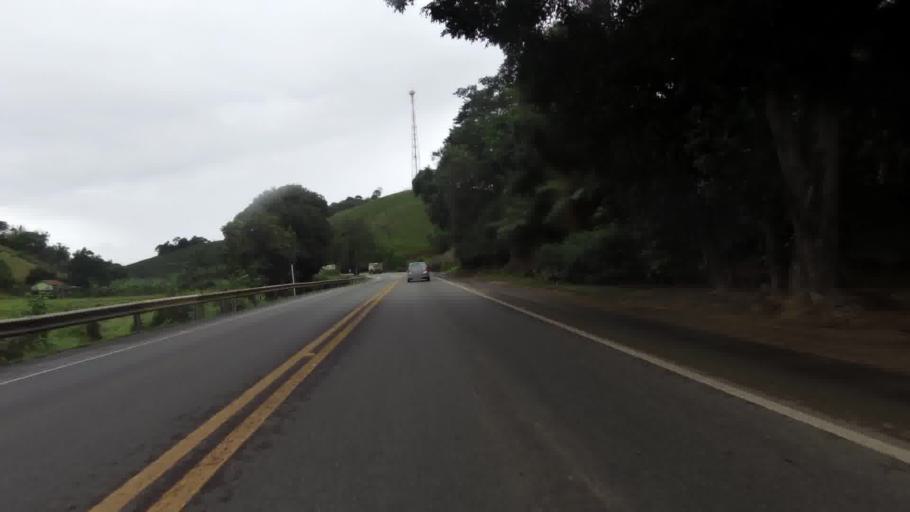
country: BR
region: Espirito Santo
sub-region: Rio Novo Do Sul
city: Rio Novo do Sul
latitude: -20.8384
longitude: -40.8701
